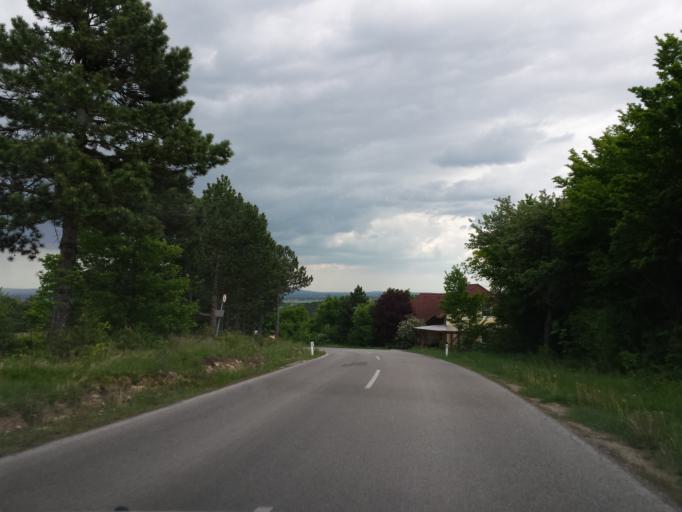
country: AT
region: Lower Austria
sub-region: Politischer Bezirk Baden
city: Hirtenberg
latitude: 47.9114
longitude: 16.1632
